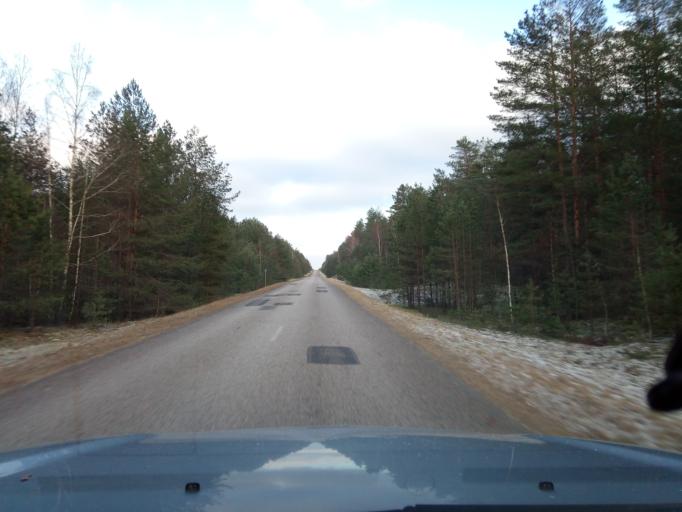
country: LT
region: Alytaus apskritis
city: Varena
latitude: 54.0866
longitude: 24.4082
